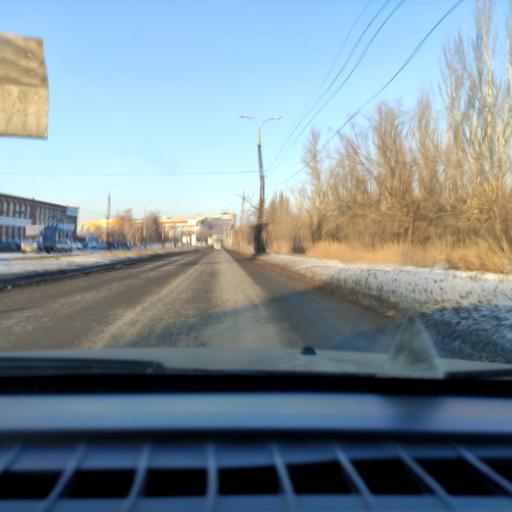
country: RU
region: Samara
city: Tol'yatti
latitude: 53.5563
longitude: 49.3042
